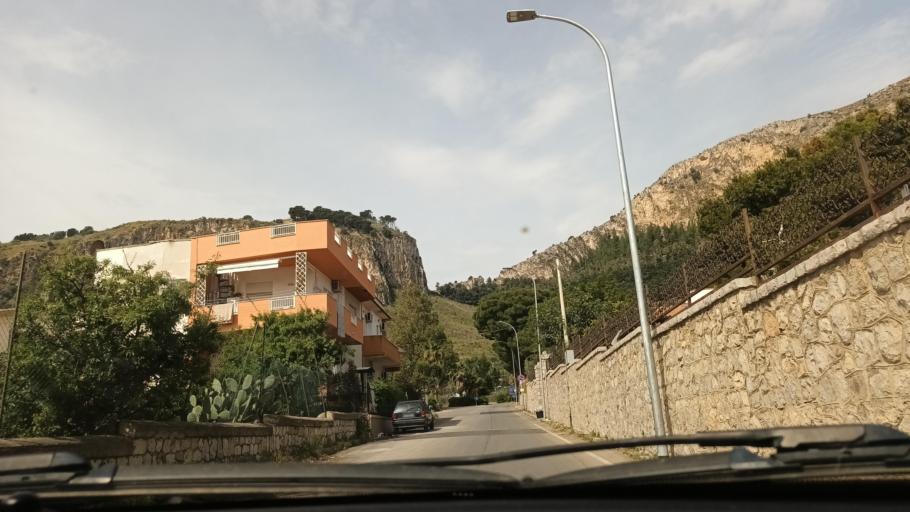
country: IT
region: Sicily
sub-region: Palermo
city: Santa Flavia
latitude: 38.0974
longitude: 13.5369
